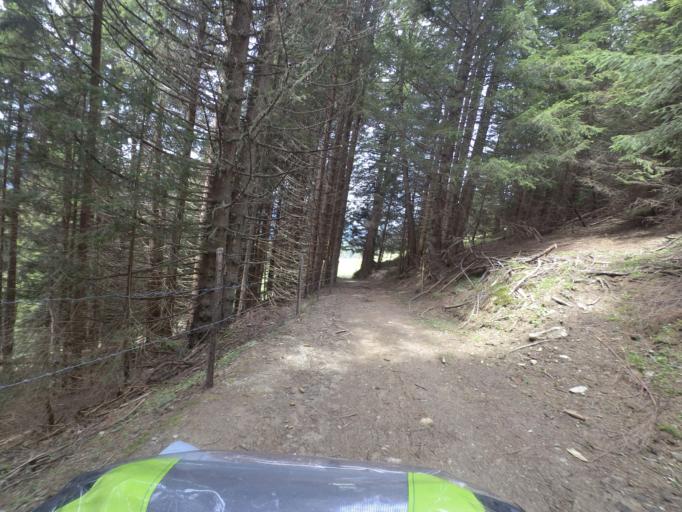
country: AT
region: Salzburg
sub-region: Politischer Bezirk Sankt Johann im Pongau
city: Dorfgastein
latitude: 47.2620
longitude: 13.1221
